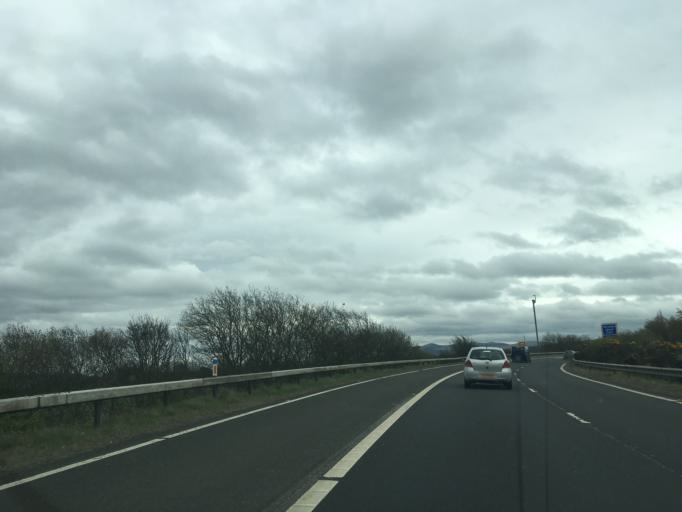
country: GB
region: Scotland
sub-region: Edinburgh
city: Kirkliston
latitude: 55.9459
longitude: -3.4056
